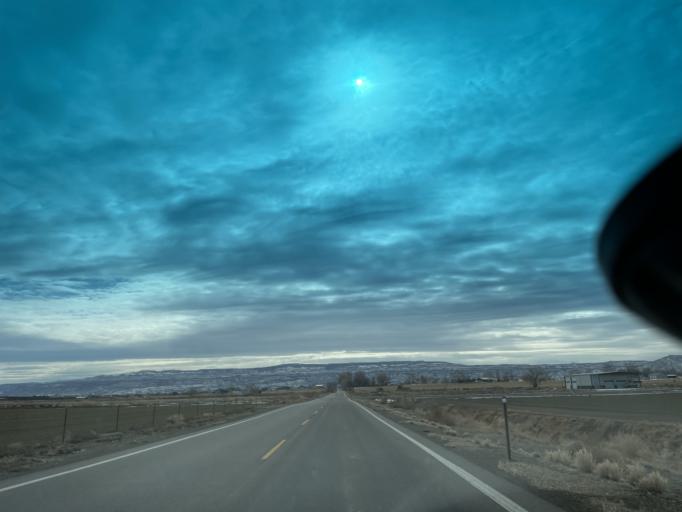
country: US
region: Colorado
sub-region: Mesa County
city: Loma
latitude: 39.2310
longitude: -108.8130
